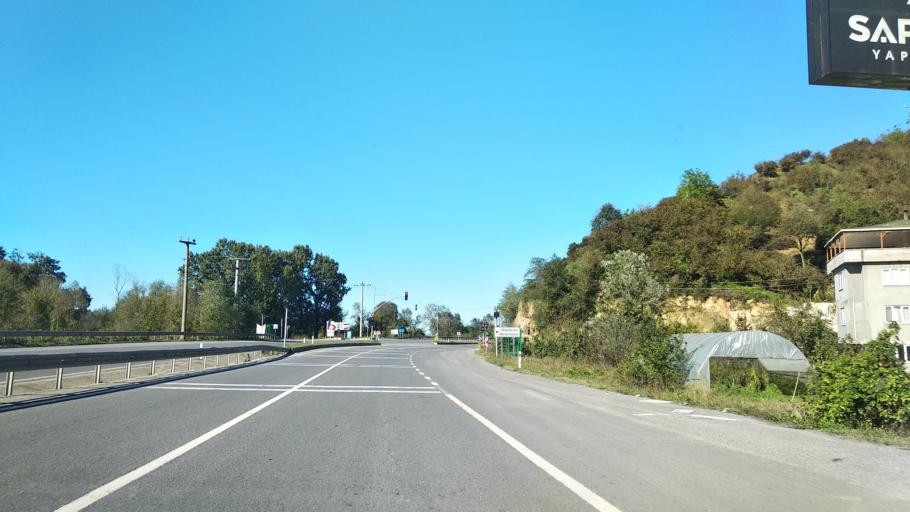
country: TR
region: Sakarya
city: Karasu
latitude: 41.0797
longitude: 30.6459
